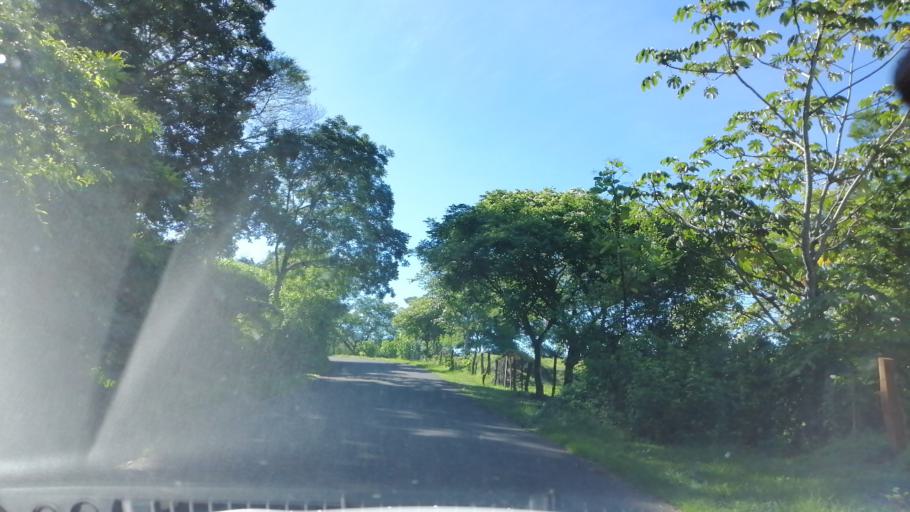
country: SV
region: Morazan
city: Corinto
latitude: 13.7905
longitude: -88.0191
